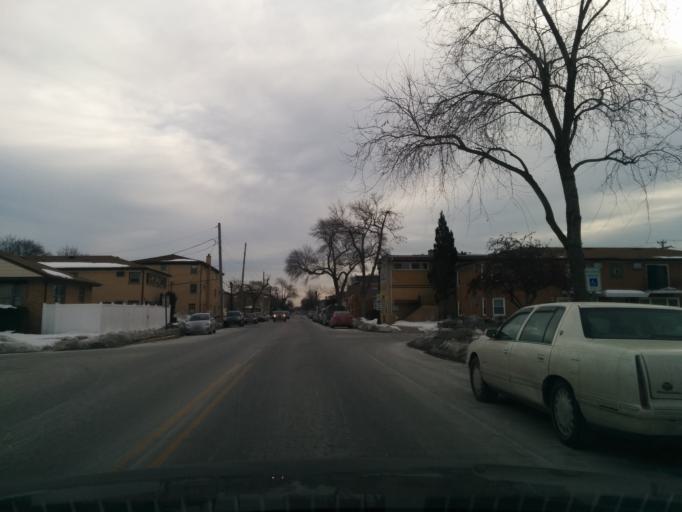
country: US
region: Illinois
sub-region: Cook County
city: Elmwood Park
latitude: 41.9233
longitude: -87.8176
